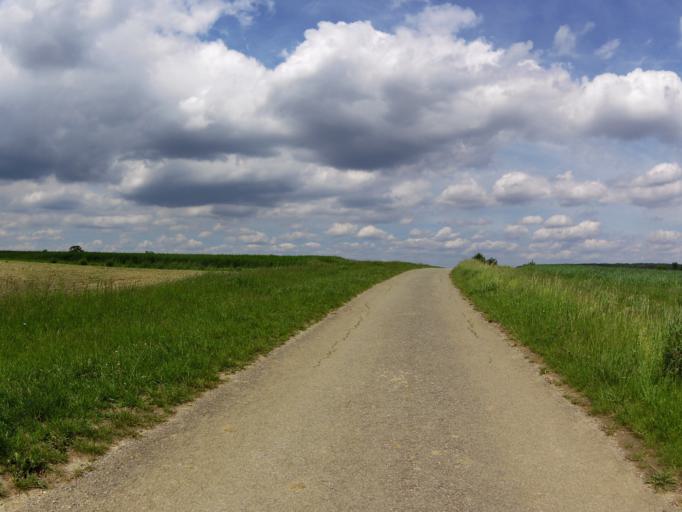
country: DE
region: Bavaria
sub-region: Regierungsbezirk Unterfranken
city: Sommerhausen
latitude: 49.7250
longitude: 10.0322
